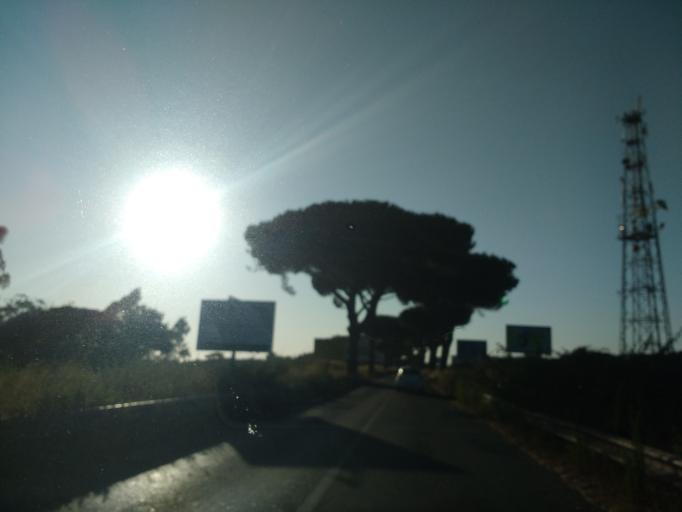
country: IT
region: Latium
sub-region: Citta metropolitana di Roma Capitale
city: Vitinia
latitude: 41.7660
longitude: 12.3815
